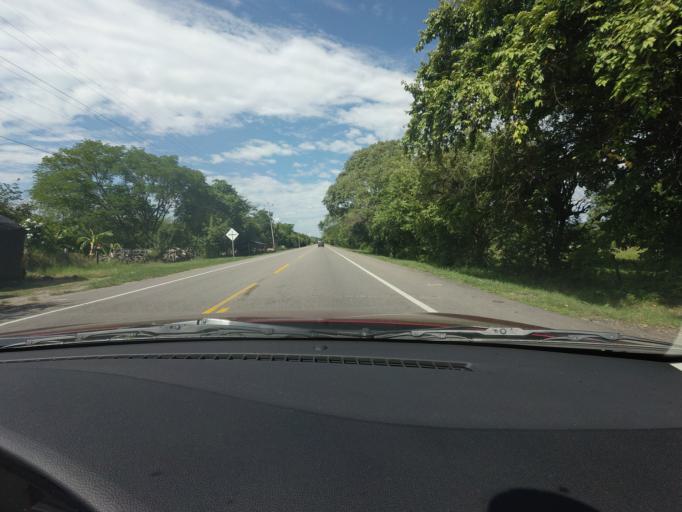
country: CO
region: Tolima
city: Coyaima
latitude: 3.7503
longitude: -75.0755
